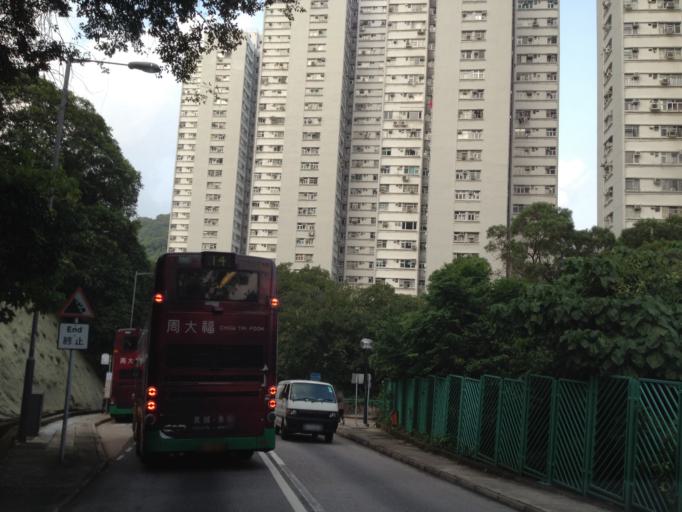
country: HK
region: Wanchai
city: Wan Chai
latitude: 22.2687
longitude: 114.2326
